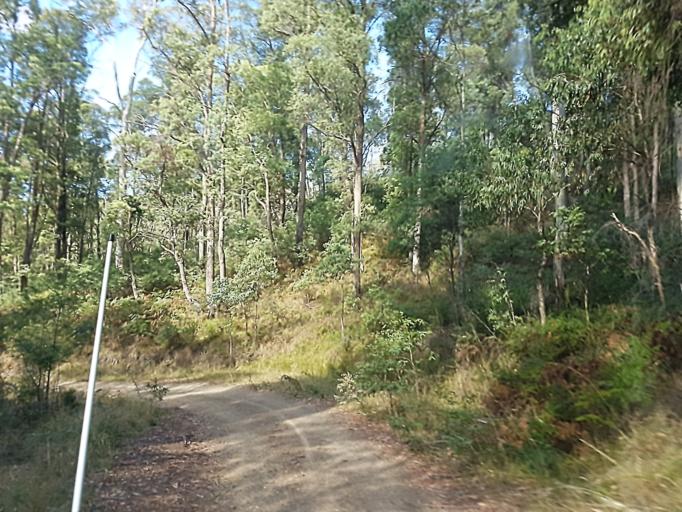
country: AU
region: Victoria
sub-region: Alpine
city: Mount Beauty
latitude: -36.9160
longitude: 147.0452
